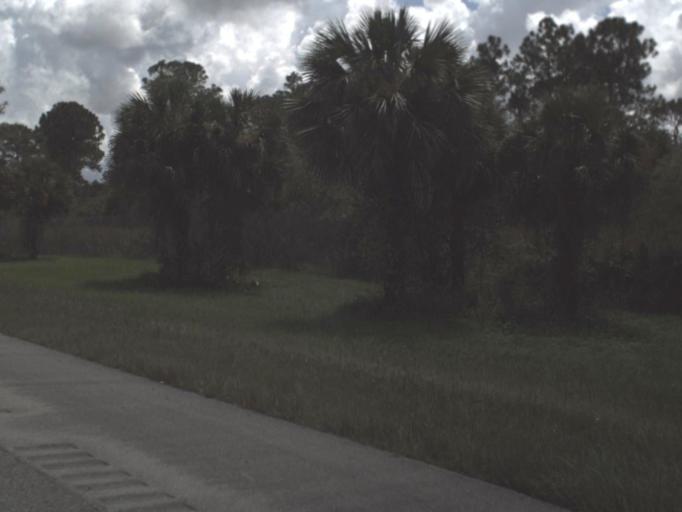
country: US
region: Florida
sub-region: Collier County
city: Orangetree
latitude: 26.1530
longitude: -81.4770
